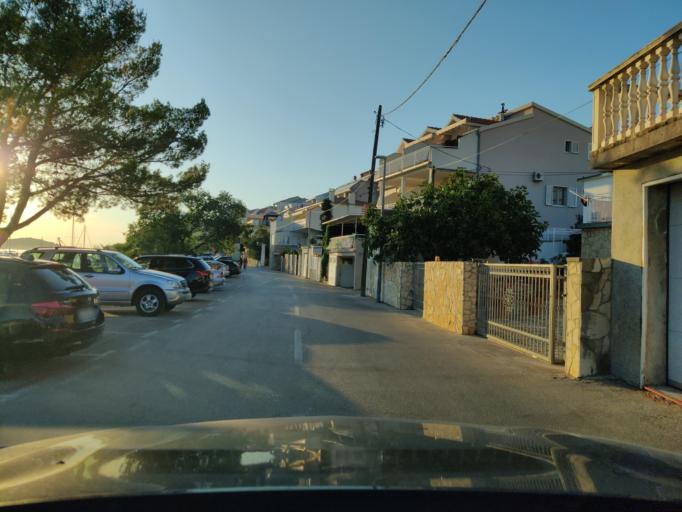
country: HR
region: Sibensko-Kniniska
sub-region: Grad Sibenik
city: Tisno
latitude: 43.8040
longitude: 15.6341
